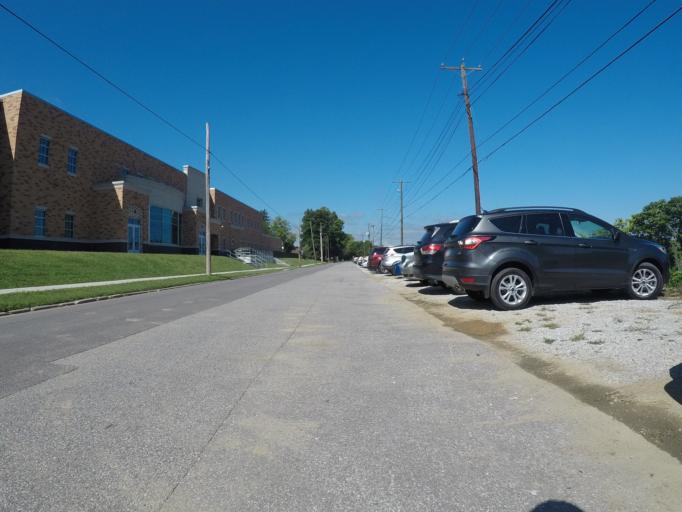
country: US
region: West Virginia
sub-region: Wayne County
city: Ceredo
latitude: 38.4002
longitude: -82.5676
